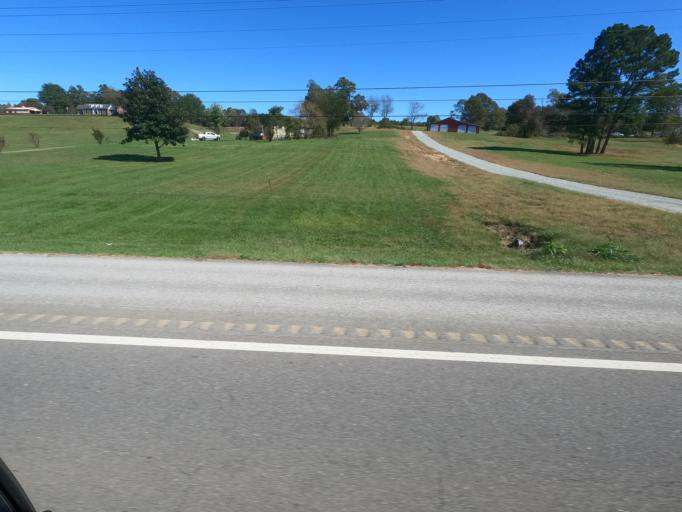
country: US
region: Tennessee
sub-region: Maury County
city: Mount Pleasant
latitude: 35.3962
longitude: -87.2780
